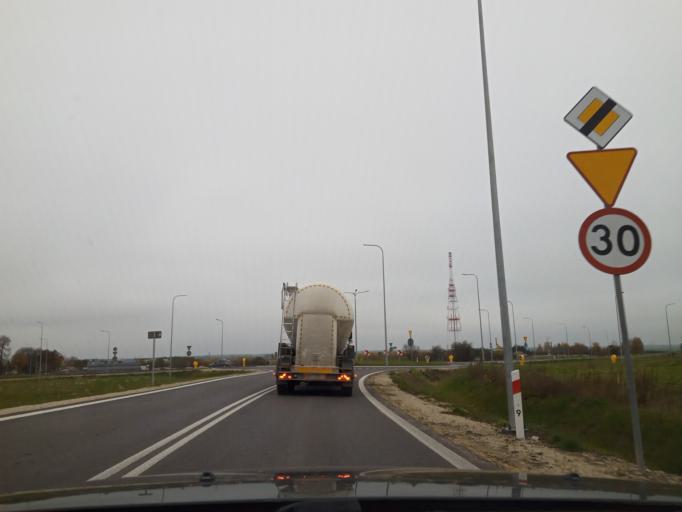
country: PL
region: Swietokrzyskie
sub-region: Powiat jedrzejowski
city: Jedrzejow
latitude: 50.6183
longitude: 20.3124
